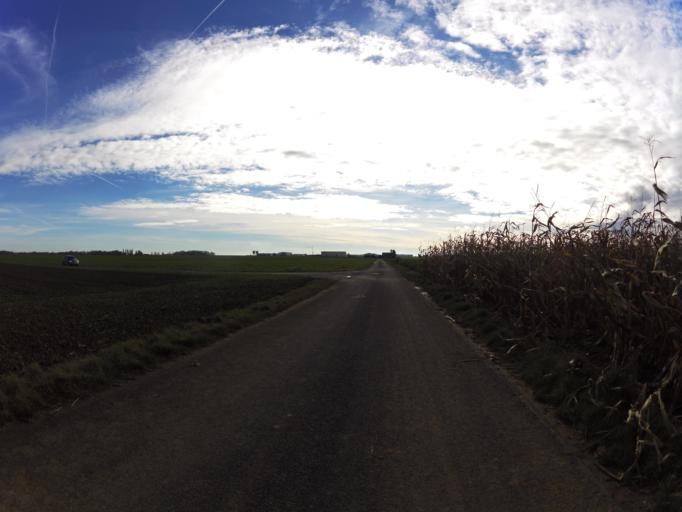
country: DE
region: Bavaria
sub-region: Regierungsbezirk Unterfranken
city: Giebelstadt
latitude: 49.6631
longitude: 9.9521
